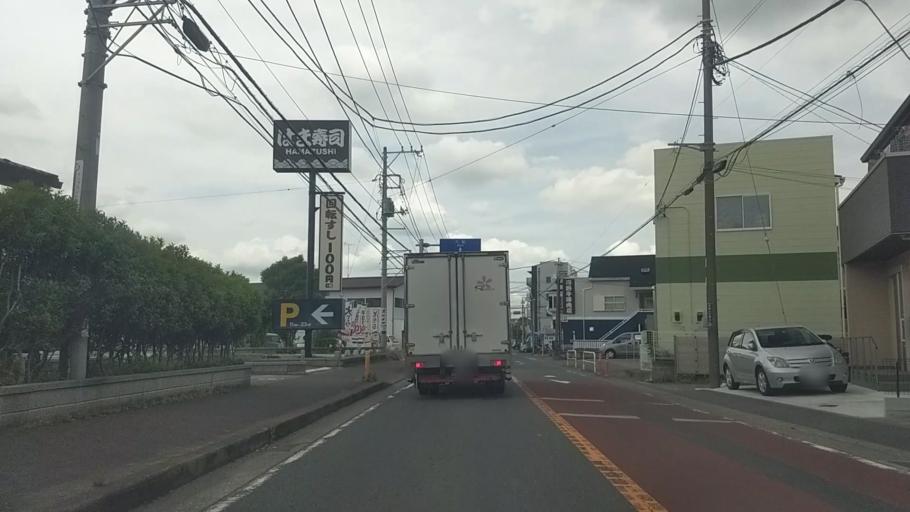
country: JP
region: Kanagawa
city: Fujisawa
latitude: 35.3298
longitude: 139.5095
